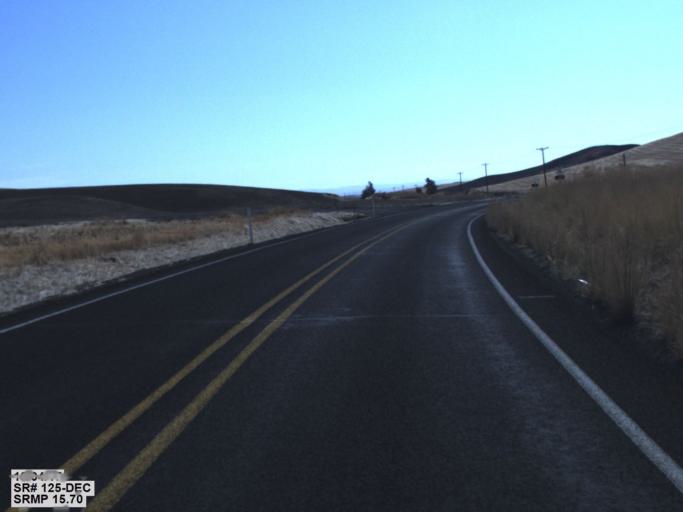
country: US
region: Washington
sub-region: Walla Walla County
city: Walla Walla
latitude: 46.1958
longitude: -118.3816
